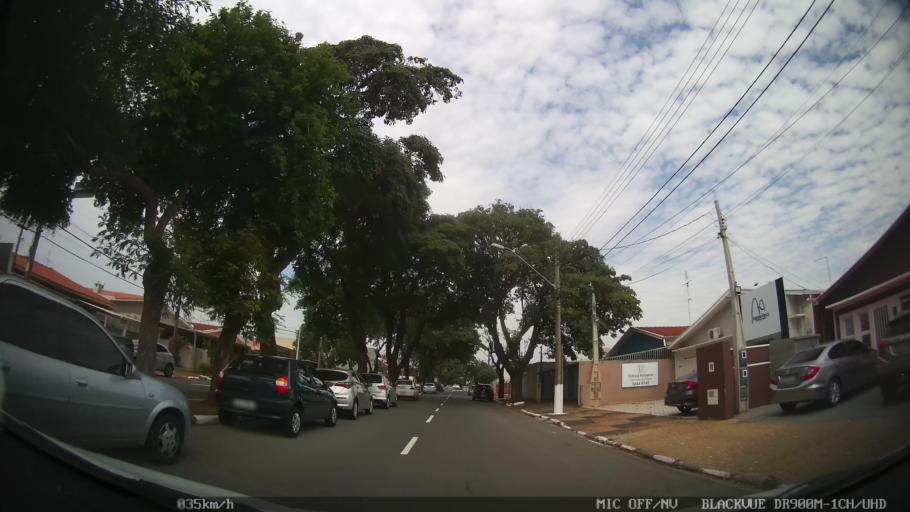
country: BR
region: Sao Paulo
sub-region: Paulinia
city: Paulinia
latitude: -22.7679
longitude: -47.1500
